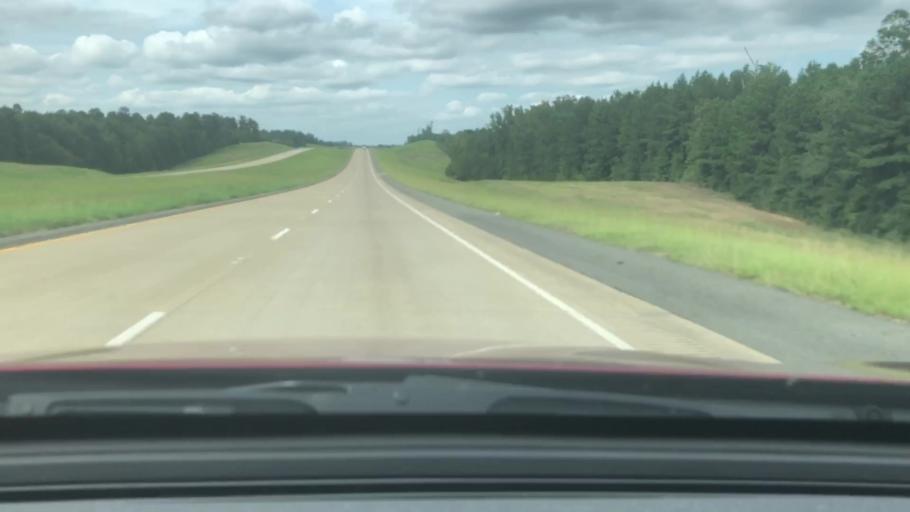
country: US
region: Louisiana
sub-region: Caddo Parish
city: Vivian
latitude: 32.9652
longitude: -93.9048
